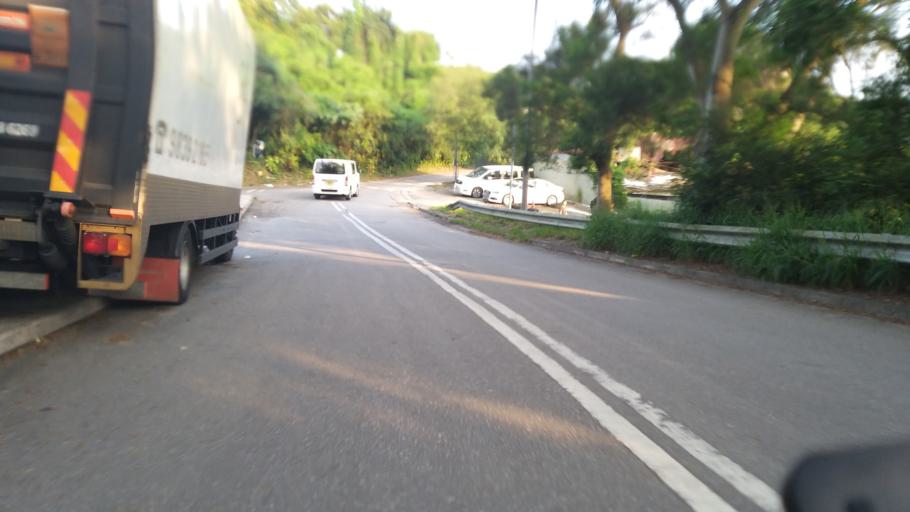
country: HK
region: Yuen Long
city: Yuen Long Kau Hui
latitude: 22.4465
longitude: 114.0137
